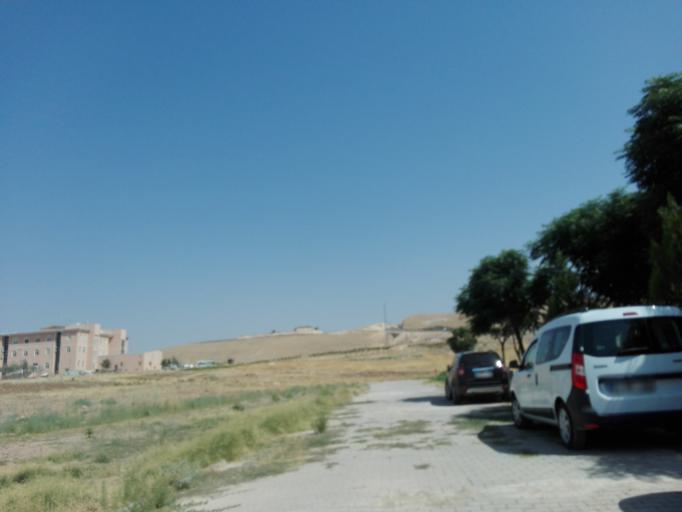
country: TR
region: Batman
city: Oymatas
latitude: 37.7918
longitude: 41.0649
